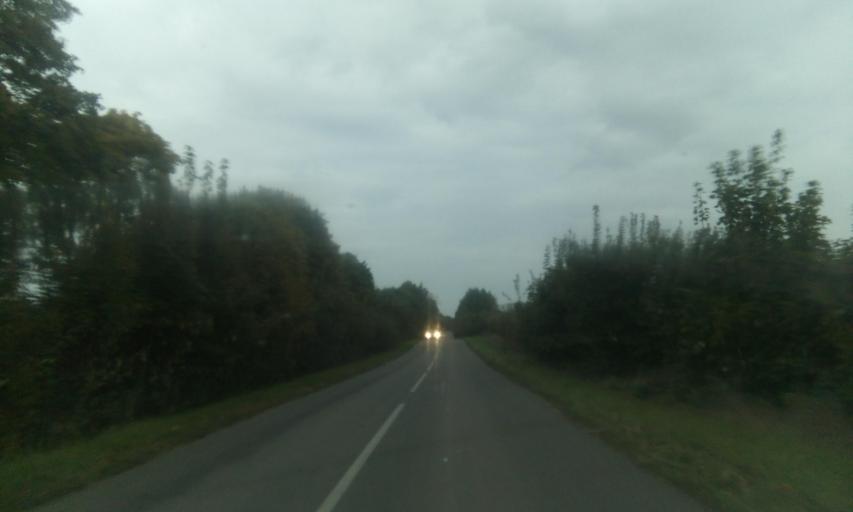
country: RU
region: Tula
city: Dubovka
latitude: 53.9586
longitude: 38.0761
